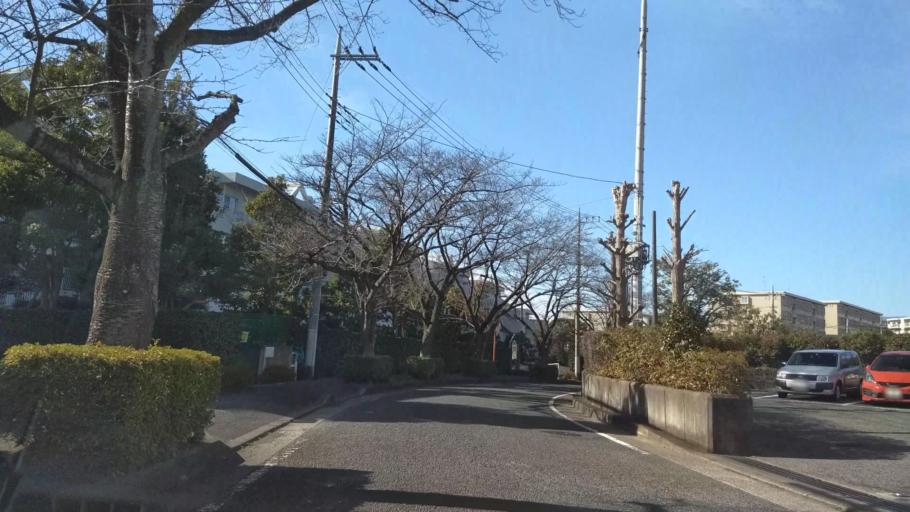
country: JP
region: Kanagawa
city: Hadano
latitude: 35.3541
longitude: 139.2274
